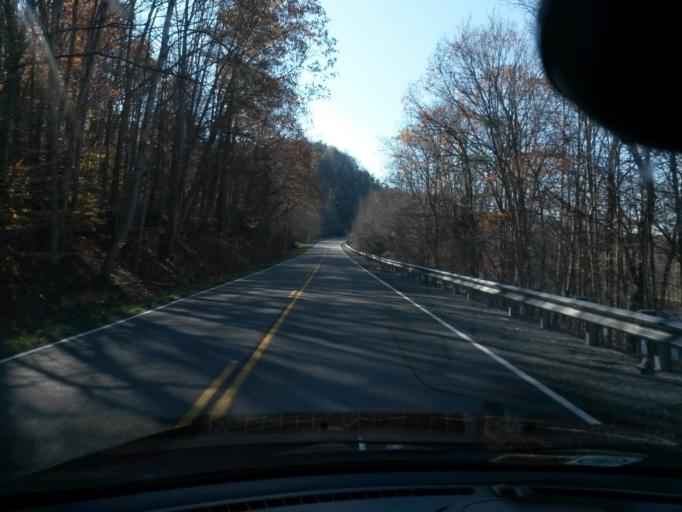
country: US
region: Virginia
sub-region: Botetourt County
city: Buchanan
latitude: 37.5862
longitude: -79.7279
